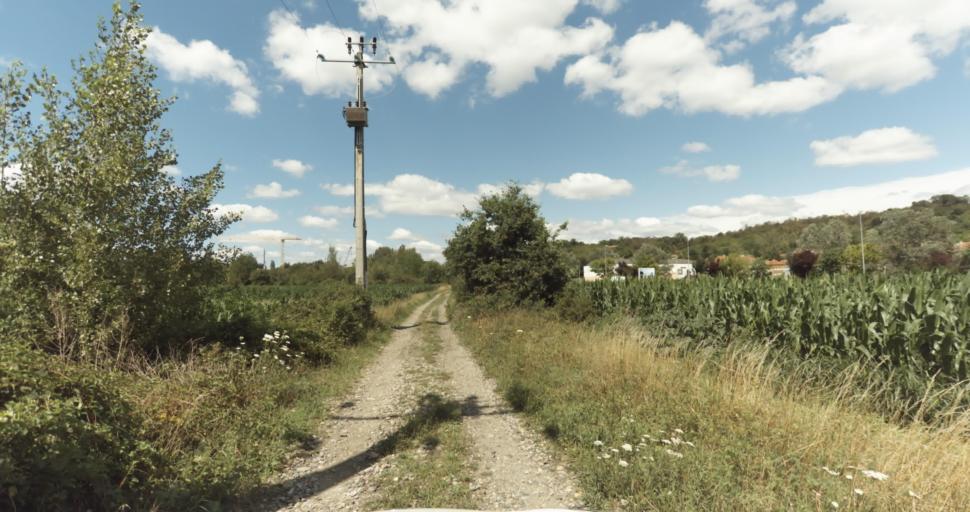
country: FR
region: Rhone-Alpes
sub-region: Departement du Rhone
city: Brignais
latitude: 45.6900
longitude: 4.7646
